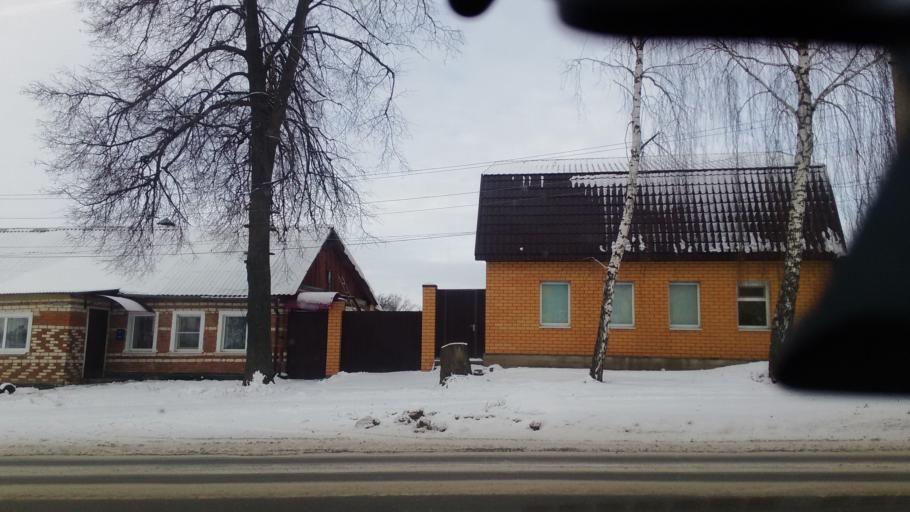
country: RU
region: Tula
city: Bogoroditsk
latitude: 53.7678
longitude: 38.1168
